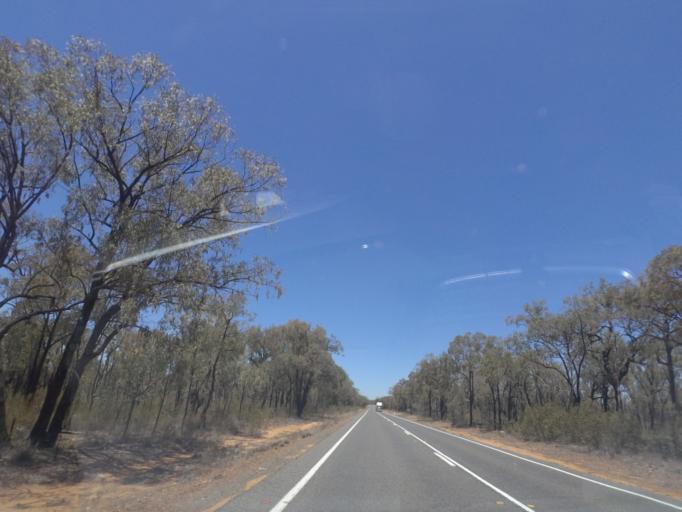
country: AU
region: New South Wales
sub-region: Narrabri
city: Narrabri
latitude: -30.7049
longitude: 149.5328
